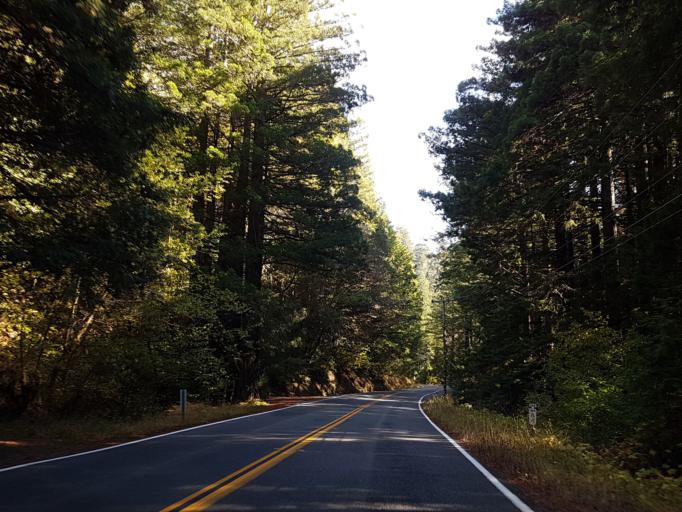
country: US
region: California
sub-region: Humboldt County
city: Rio Dell
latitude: 40.4091
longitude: -123.9547
